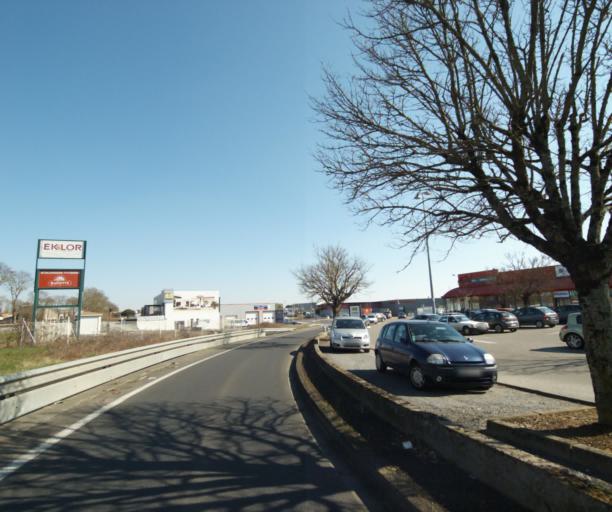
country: FR
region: Poitou-Charentes
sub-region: Departement des Deux-Sevres
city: Chauray
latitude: 46.3424
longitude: -0.3825
